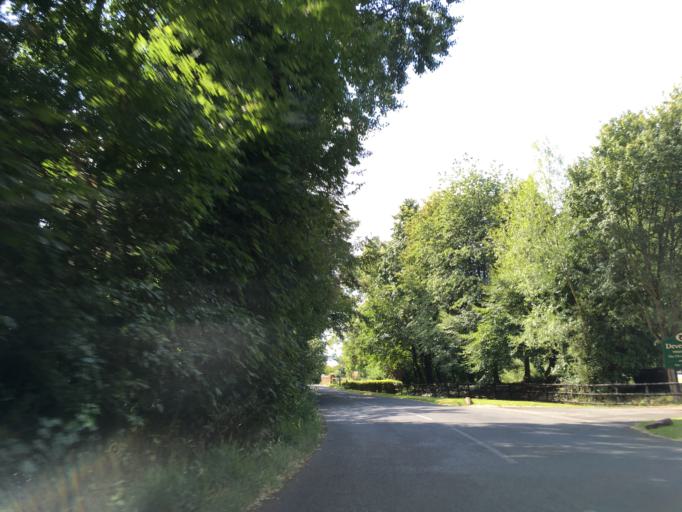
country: GB
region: England
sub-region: Hampshire
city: Kings Worthy
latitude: 51.1749
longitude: -1.3757
